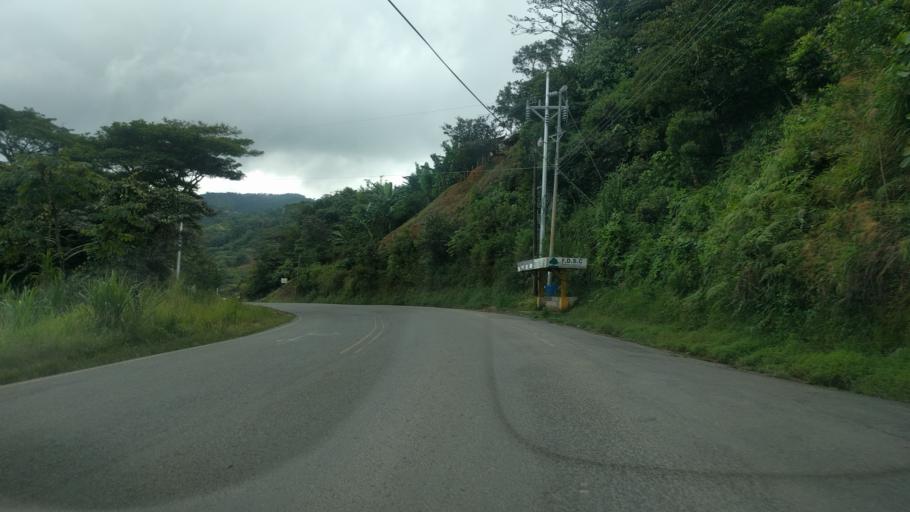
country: CR
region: Alajuela
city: San Rafael
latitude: 10.0311
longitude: -84.5117
